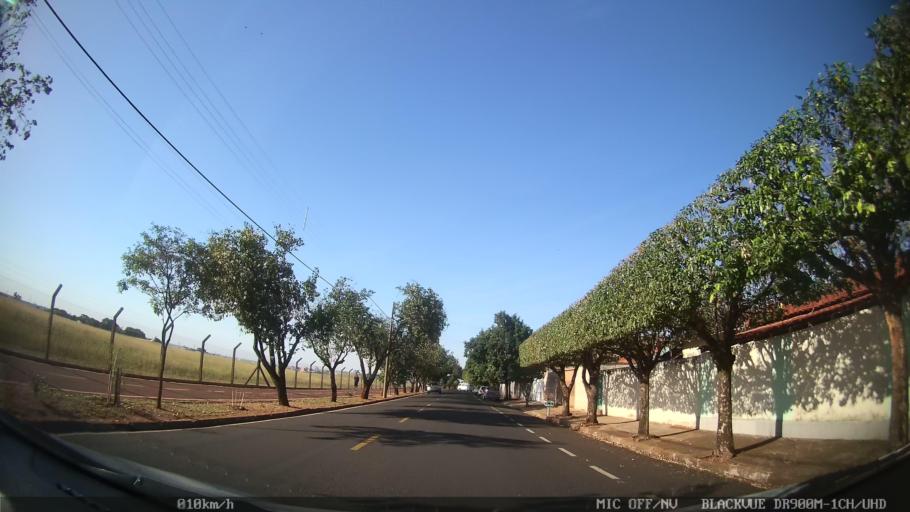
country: BR
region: Sao Paulo
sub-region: Sao Jose Do Rio Preto
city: Sao Jose do Rio Preto
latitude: -20.8183
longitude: -49.4063
